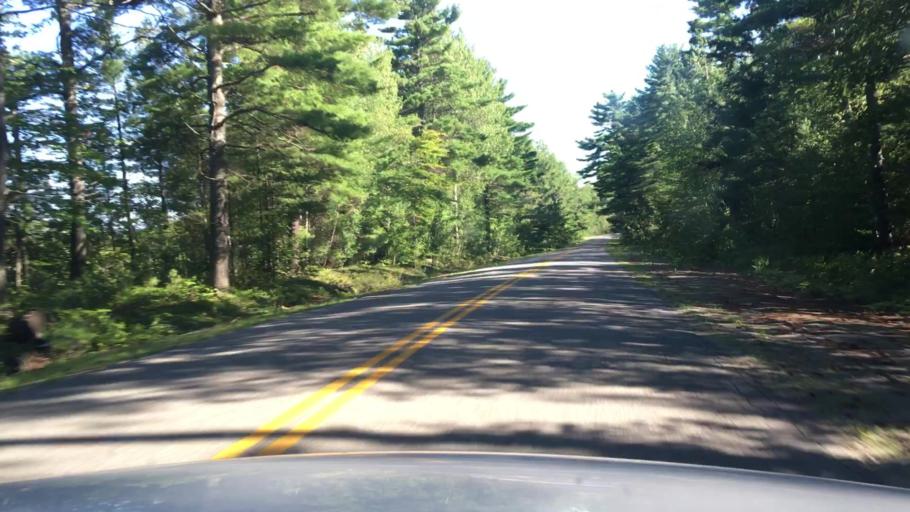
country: US
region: Maine
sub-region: Penobscot County
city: Enfield
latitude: 45.2292
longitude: -68.5802
